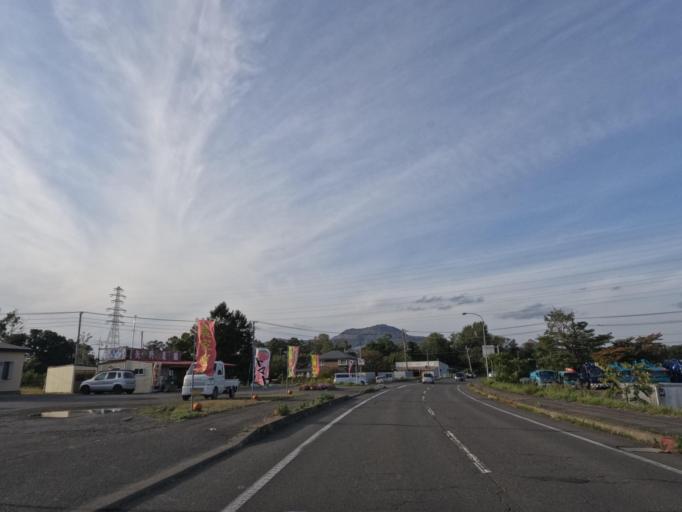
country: JP
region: Hokkaido
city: Date
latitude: 42.4878
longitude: 140.8732
